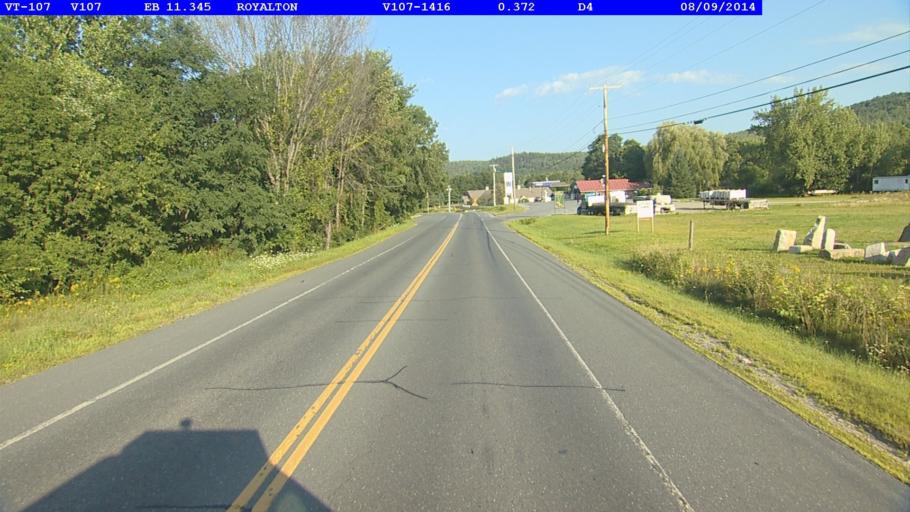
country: US
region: Vermont
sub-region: Orange County
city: Randolph
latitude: 43.8244
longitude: -72.6077
